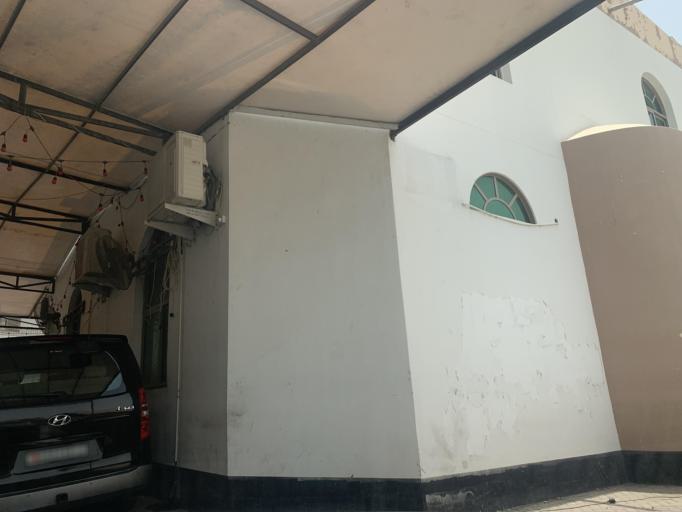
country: BH
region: Manama
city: Jidd Hafs
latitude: 26.2090
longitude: 50.5437
